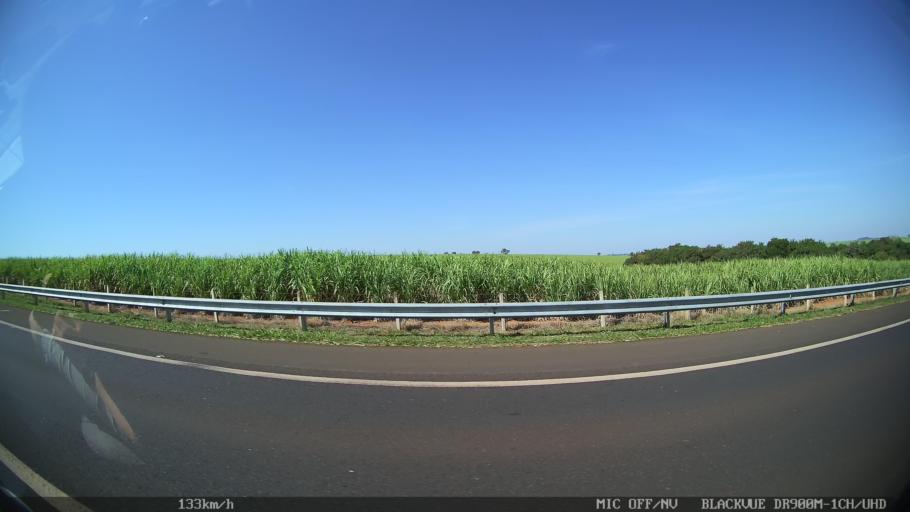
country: BR
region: Sao Paulo
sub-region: Batatais
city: Batatais
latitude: -20.8222
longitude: -47.5904
